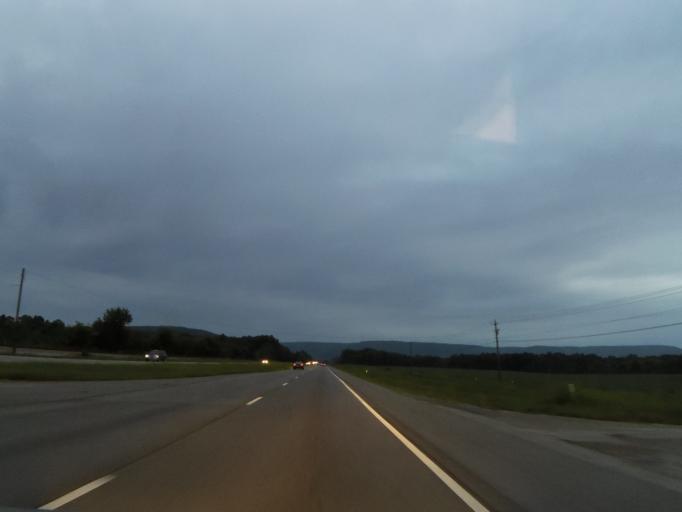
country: US
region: Alabama
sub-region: Madison County
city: Owens Cross Roads
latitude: 34.7263
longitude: -86.4170
